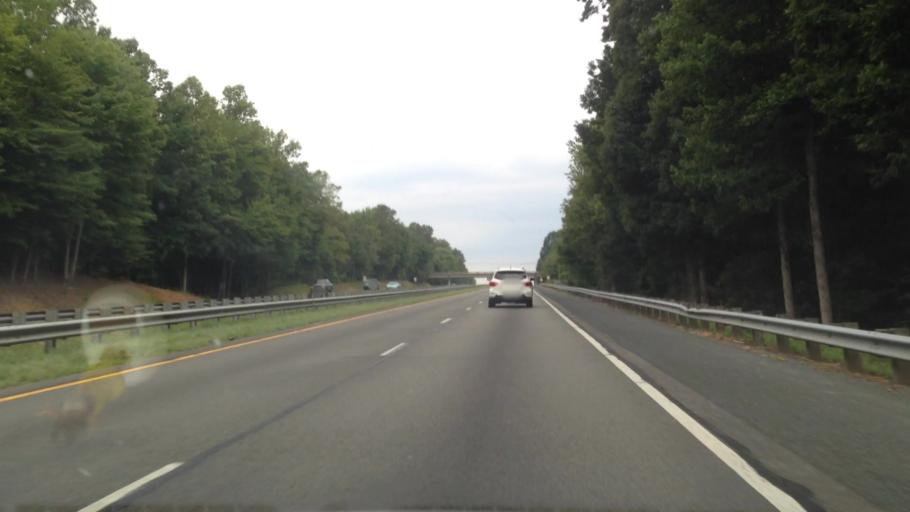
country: US
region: North Carolina
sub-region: Stokes County
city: King
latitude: 36.2810
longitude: -80.3886
